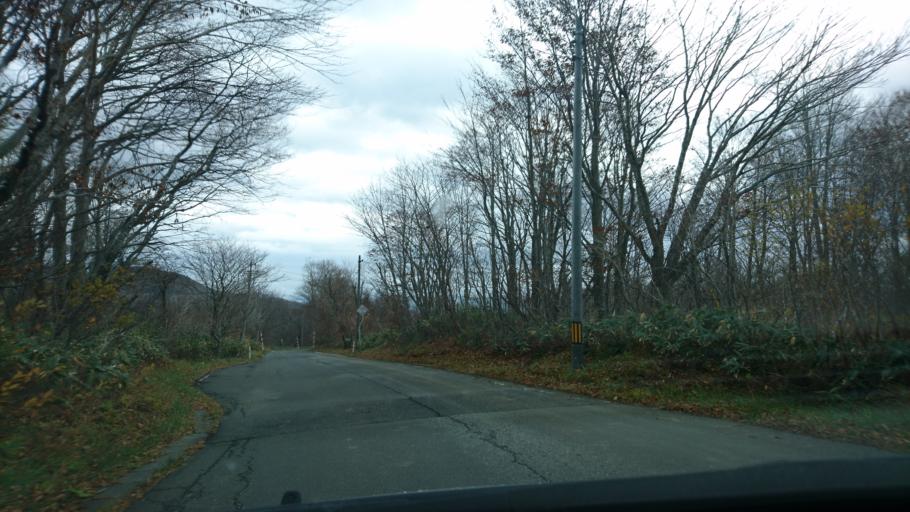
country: JP
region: Iwate
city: Ichinoseki
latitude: 38.9268
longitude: 140.8408
